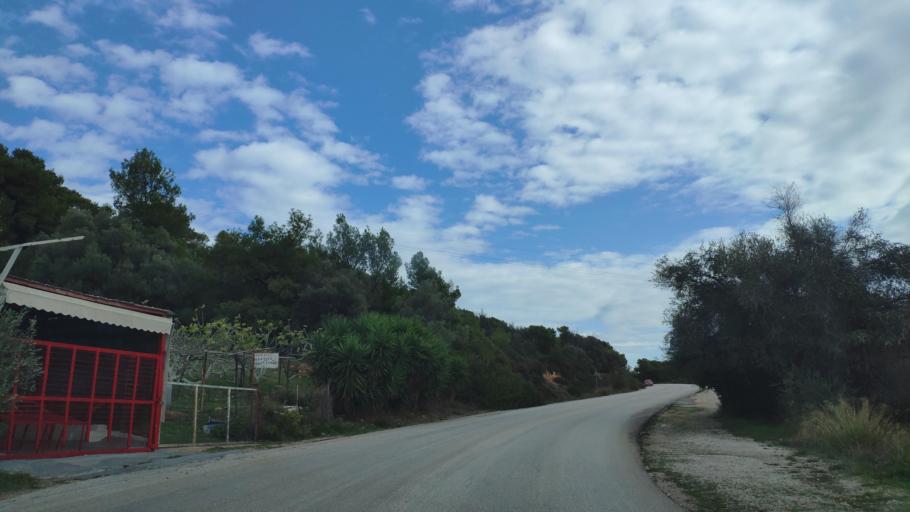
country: GR
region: Attica
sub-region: Nomarchia Anatolikis Attikis
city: Artemida
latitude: 37.9289
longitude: 24.0002
